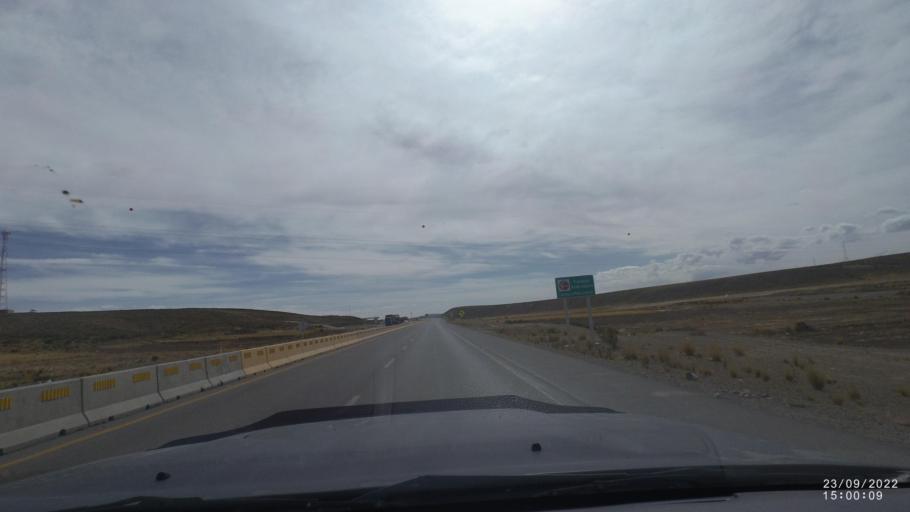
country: BO
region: La Paz
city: Colquiri
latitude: -17.6657
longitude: -67.0423
